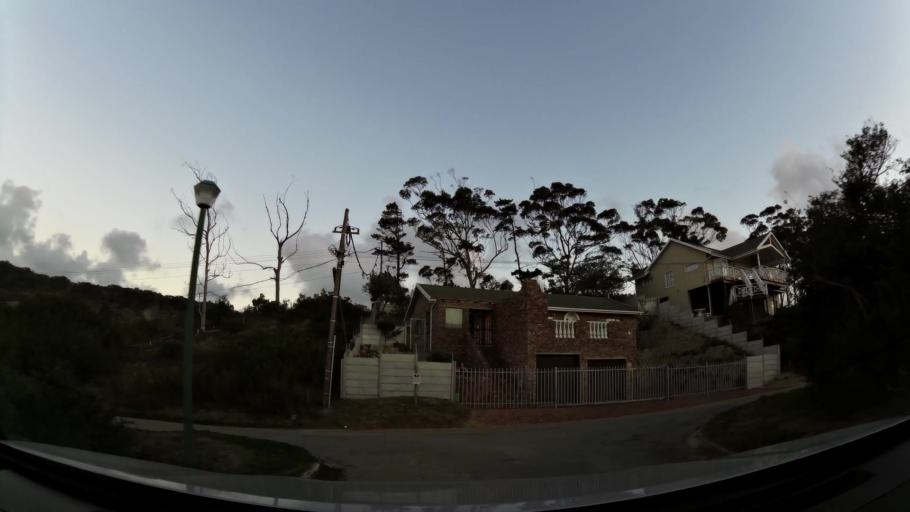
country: ZA
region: Western Cape
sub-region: Eden District Municipality
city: Knysna
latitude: -34.0287
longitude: 22.8097
